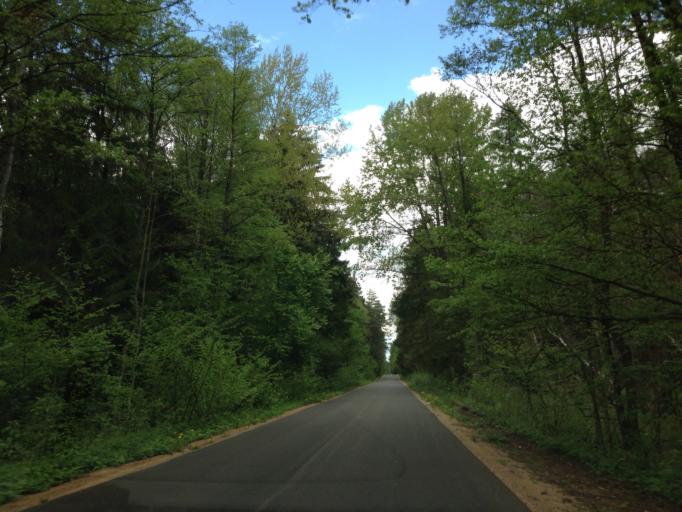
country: PL
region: Podlasie
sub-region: Powiat grajewski
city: Radzilow
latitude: 53.3394
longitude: 22.5984
